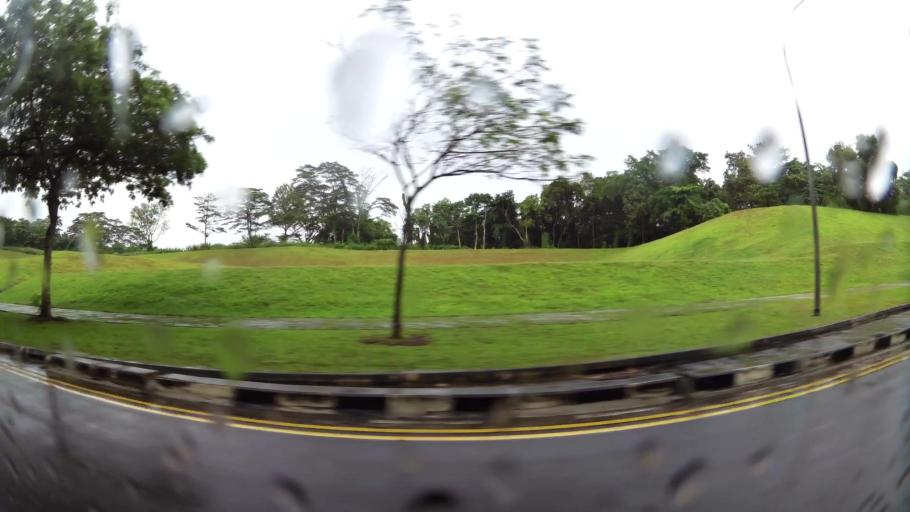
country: MY
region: Johor
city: Kampung Pasir Gudang Baru
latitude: 1.3983
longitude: 103.8804
